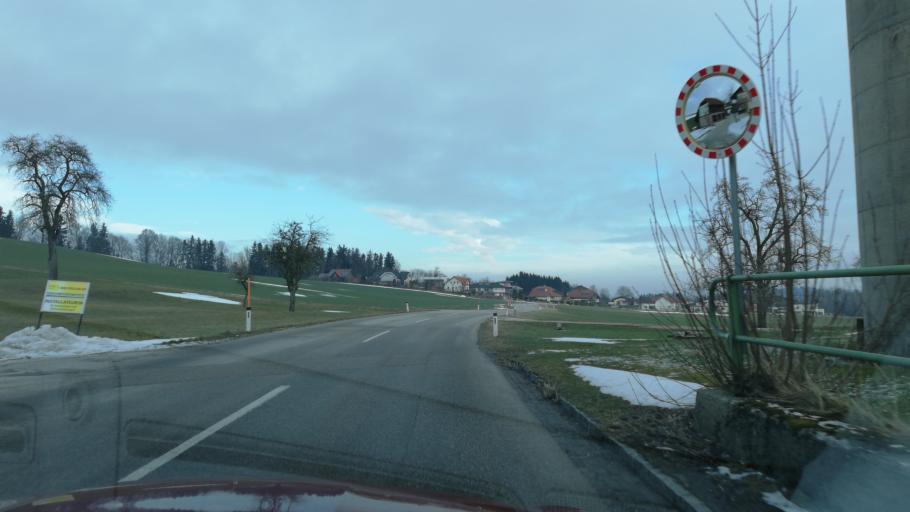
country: AT
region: Upper Austria
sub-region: Politischer Bezirk Vocklabruck
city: Wolfsegg am Hausruck
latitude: 48.1684
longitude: 13.6800
